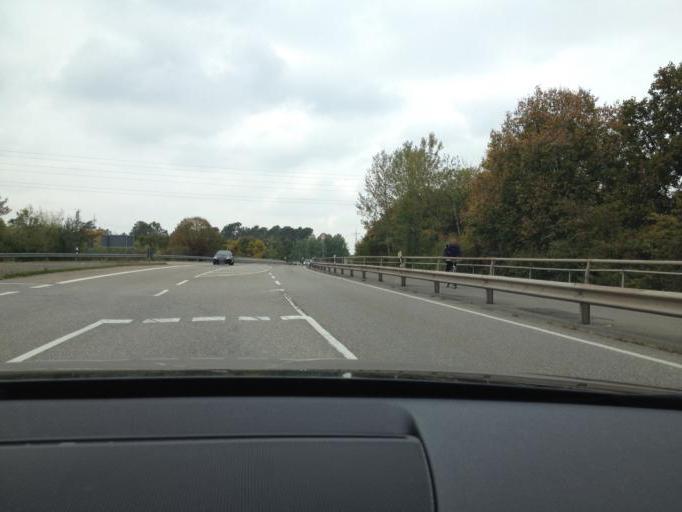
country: DE
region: Rheinland-Pfalz
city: Speyer
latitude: 49.3473
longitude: 8.4190
